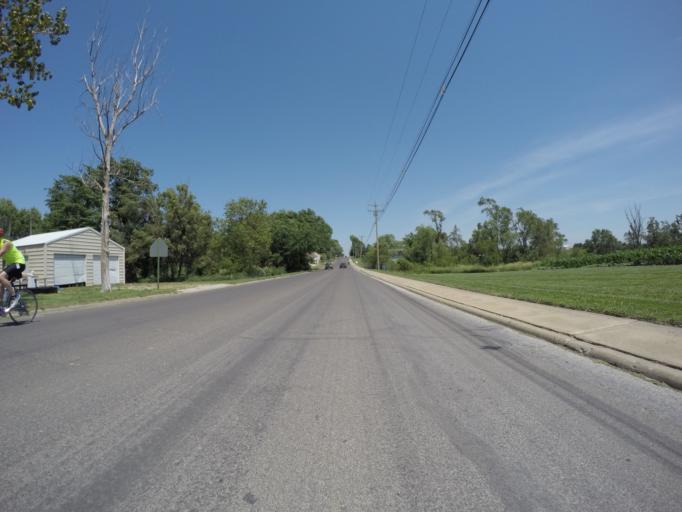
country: US
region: Kansas
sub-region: Nemaha County
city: Sabetha
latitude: 39.8997
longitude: -95.7963
